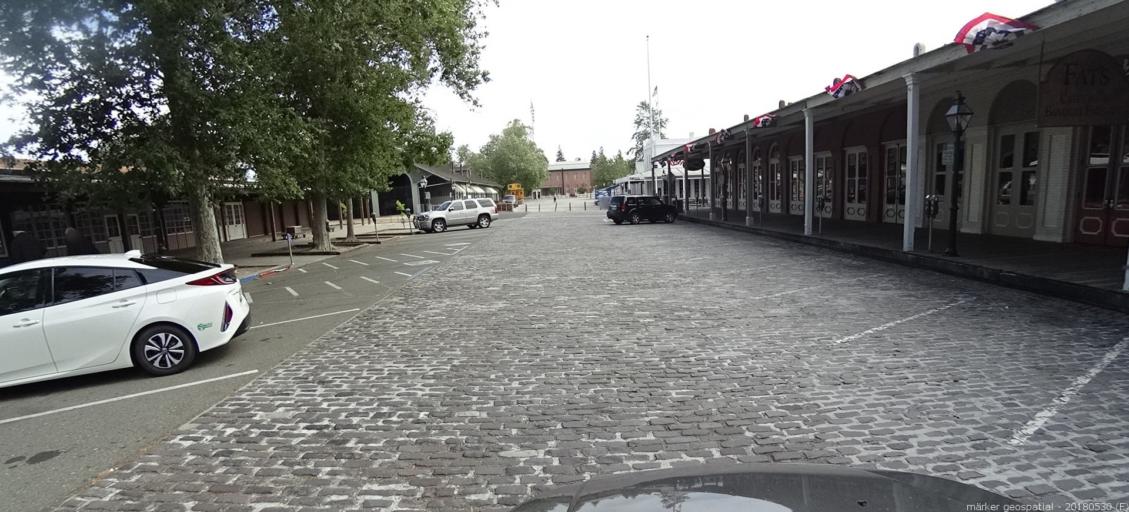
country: US
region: California
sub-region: Sacramento County
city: Sacramento
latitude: 38.5830
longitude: -121.5057
